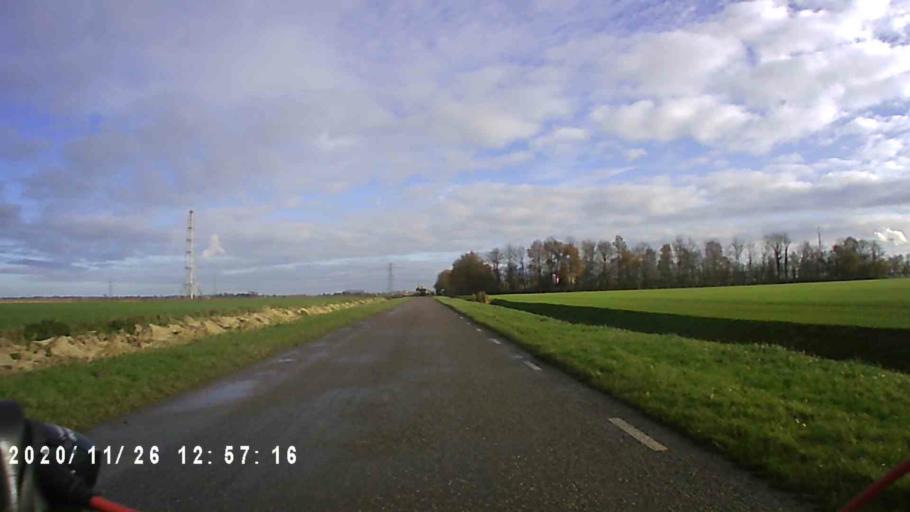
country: NL
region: Groningen
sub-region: Gemeente Appingedam
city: Appingedam
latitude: 53.3514
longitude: 6.8090
